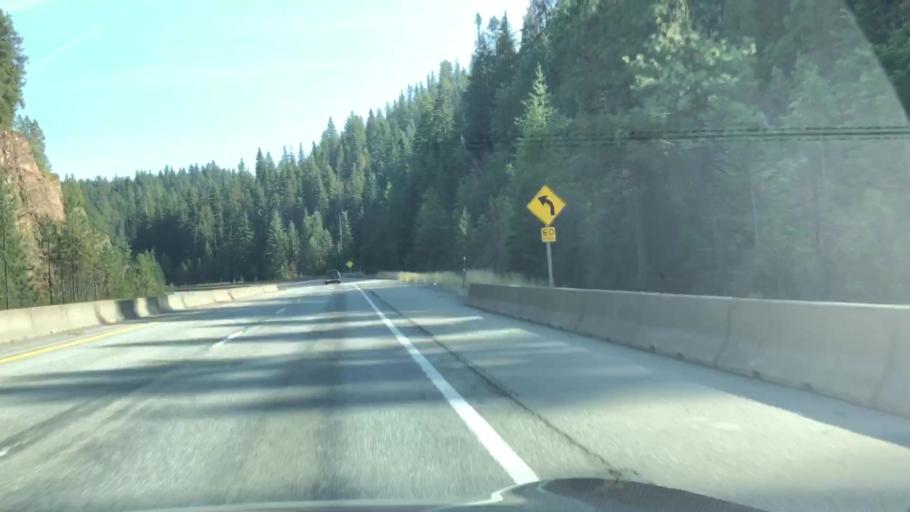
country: US
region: Idaho
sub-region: Kootenai County
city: Coeur d'Alene
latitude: 47.6227
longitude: -116.5829
